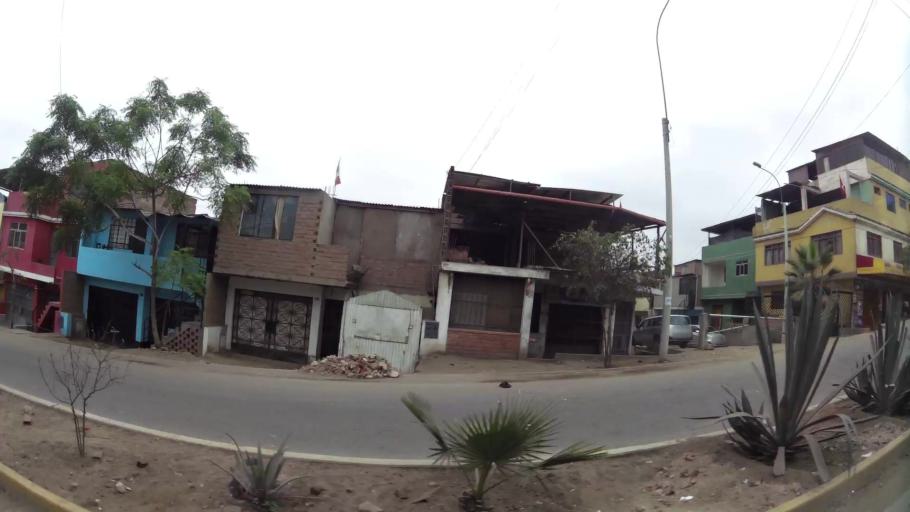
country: PE
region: Lima
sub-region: Lima
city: Surco
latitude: -12.1975
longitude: -76.9507
